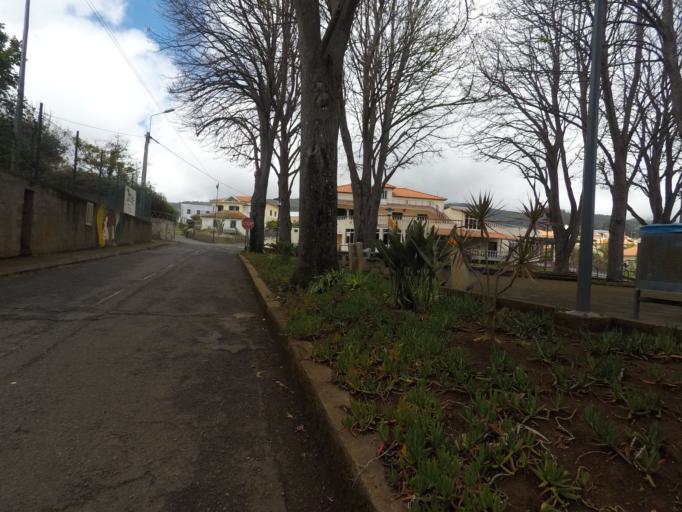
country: PT
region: Madeira
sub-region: Calheta
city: Estreito da Calheta
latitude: 32.7544
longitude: -17.2014
